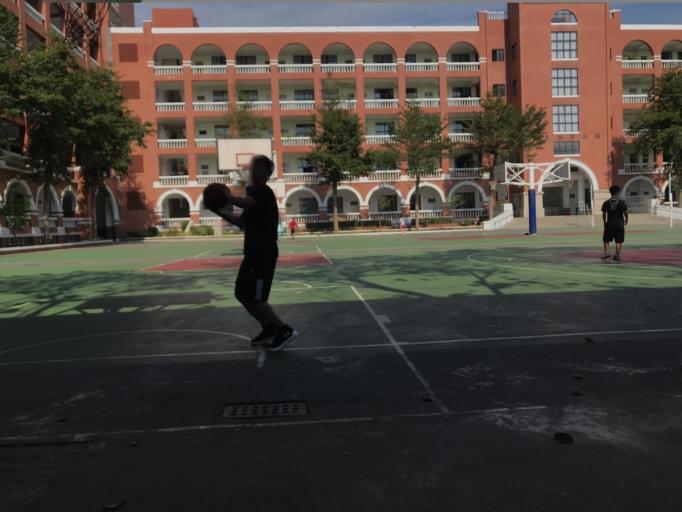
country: TW
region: Taiwan
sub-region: Tainan
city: Tainan
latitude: 22.9896
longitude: 120.2213
